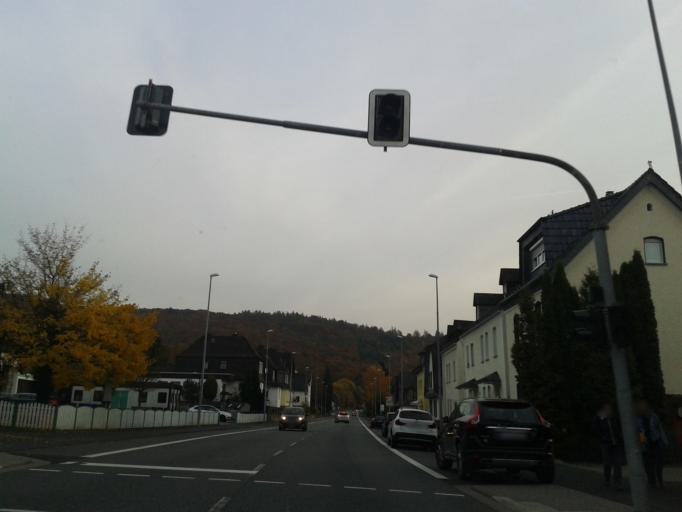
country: DE
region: Hesse
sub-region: Regierungsbezirk Giessen
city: Sinn
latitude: 50.6496
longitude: 8.3297
